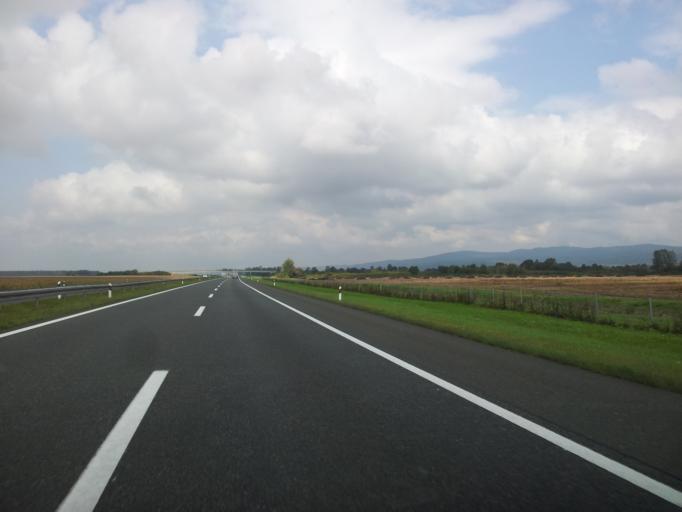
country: HR
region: Brodsko-Posavska
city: Okucani
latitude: 45.2728
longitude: 17.1334
